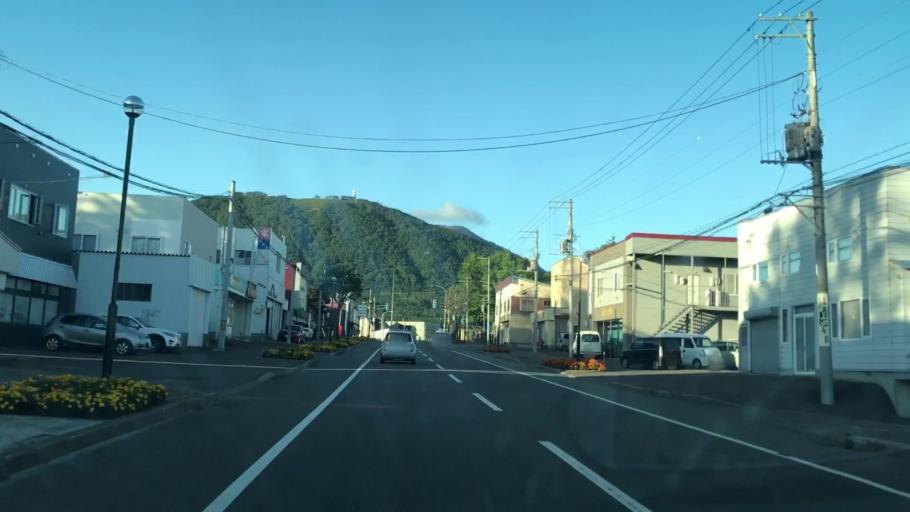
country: JP
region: Hokkaido
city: Niseko Town
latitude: 42.7363
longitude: 140.8758
